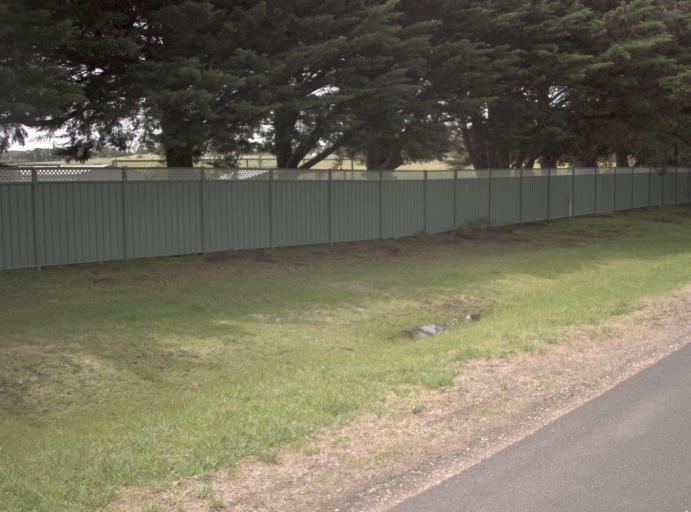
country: AU
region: Victoria
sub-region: Wellington
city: Sale
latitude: -38.0611
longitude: 147.0285
